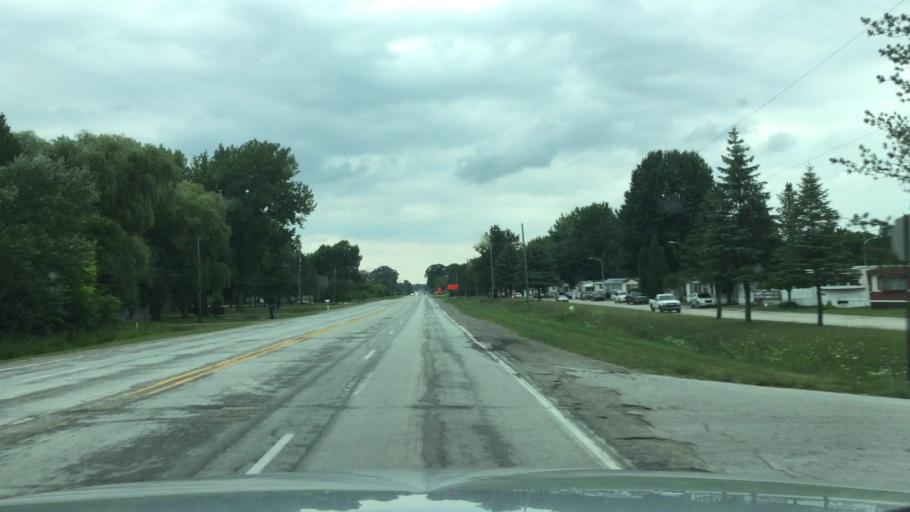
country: US
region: Michigan
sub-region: Saginaw County
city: Birch Run
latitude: 43.3168
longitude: -83.8197
